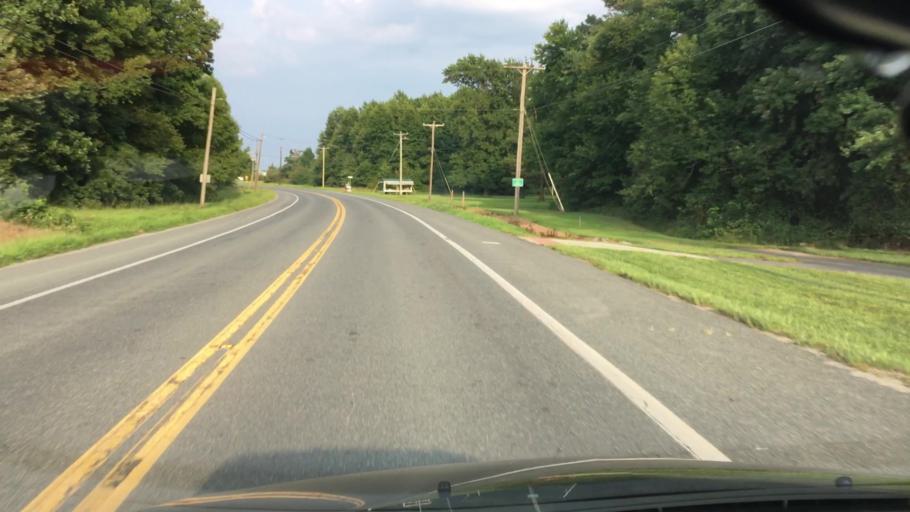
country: US
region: Delaware
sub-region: Sussex County
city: Selbyville
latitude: 38.4634
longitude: -75.1615
